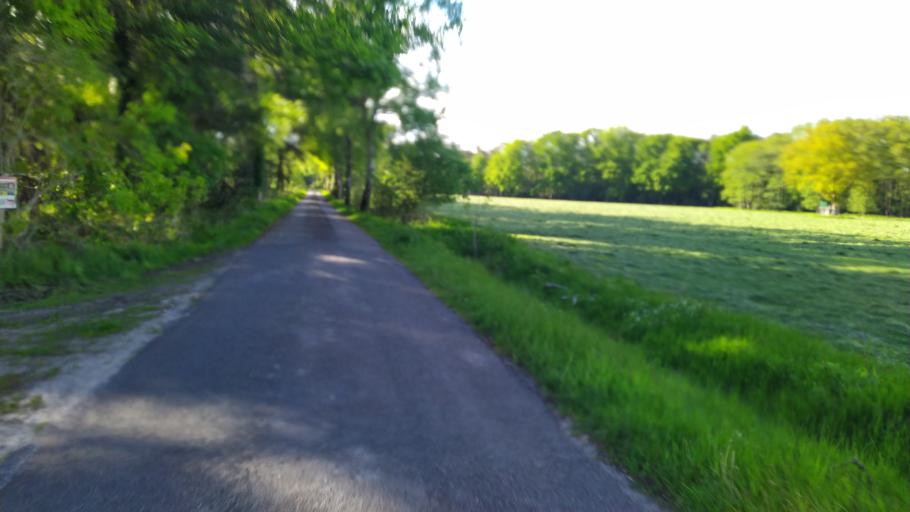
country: DE
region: Lower Saxony
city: Farven
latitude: 53.4024
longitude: 9.3515
